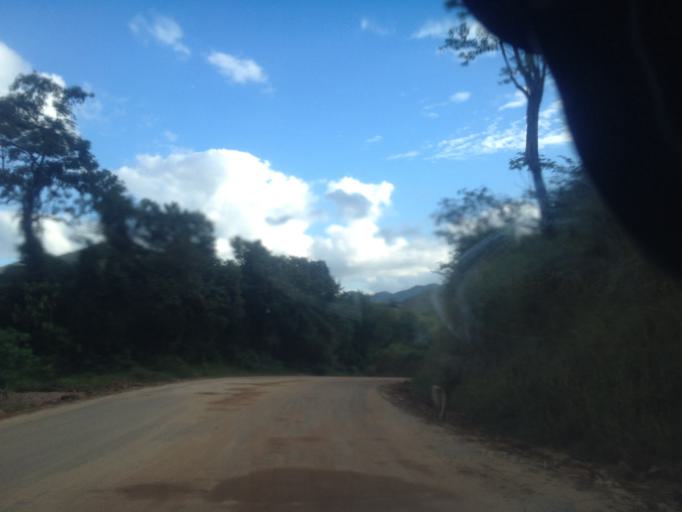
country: BR
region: Rio de Janeiro
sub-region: Quatis
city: Quatis
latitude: -22.2227
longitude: -44.2513
